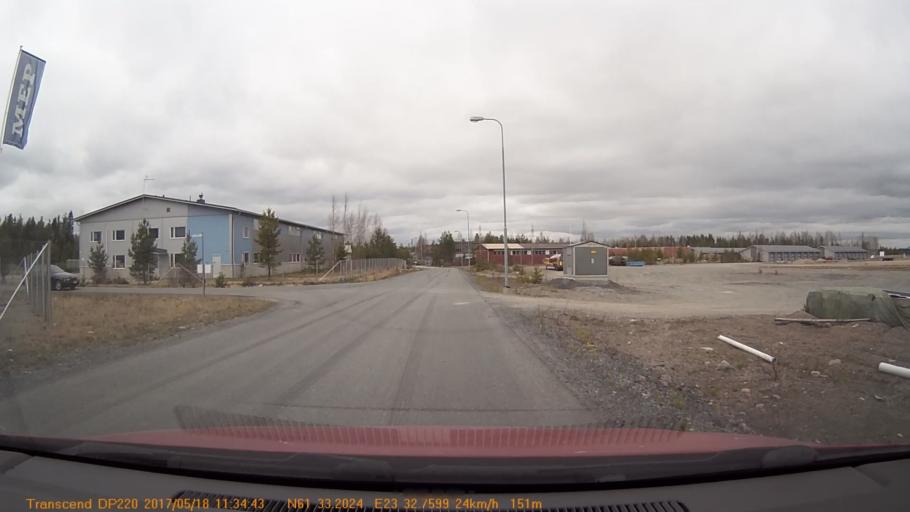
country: FI
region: Pirkanmaa
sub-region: Tampere
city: Yloejaervi
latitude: 61.5532
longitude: 23.5462
